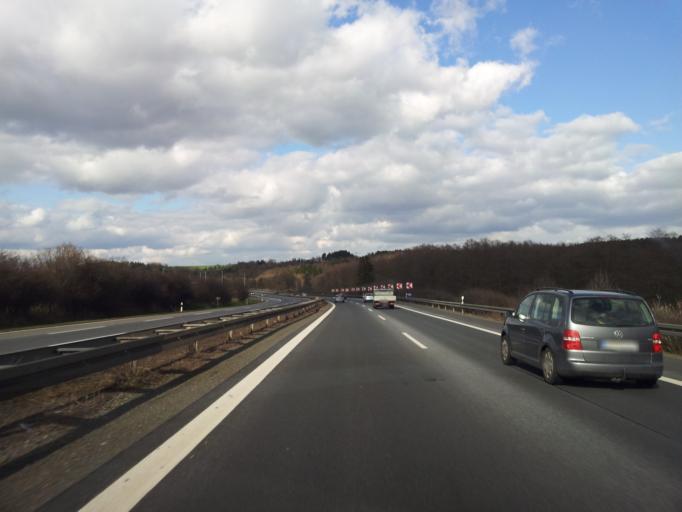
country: DE
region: Saxony
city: Theuma
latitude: 50.4614
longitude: 12.1829
